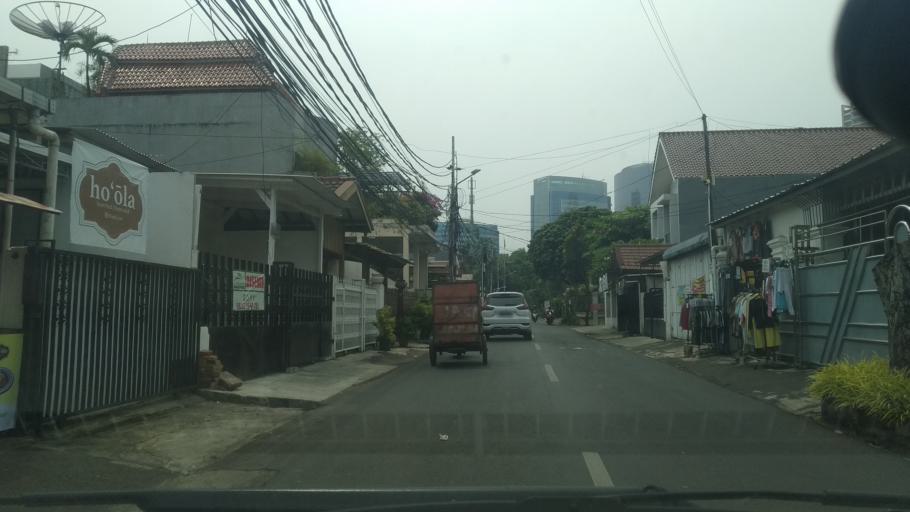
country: ID
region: Banten
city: South Tangerang
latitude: -6.2631
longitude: 106.7769
